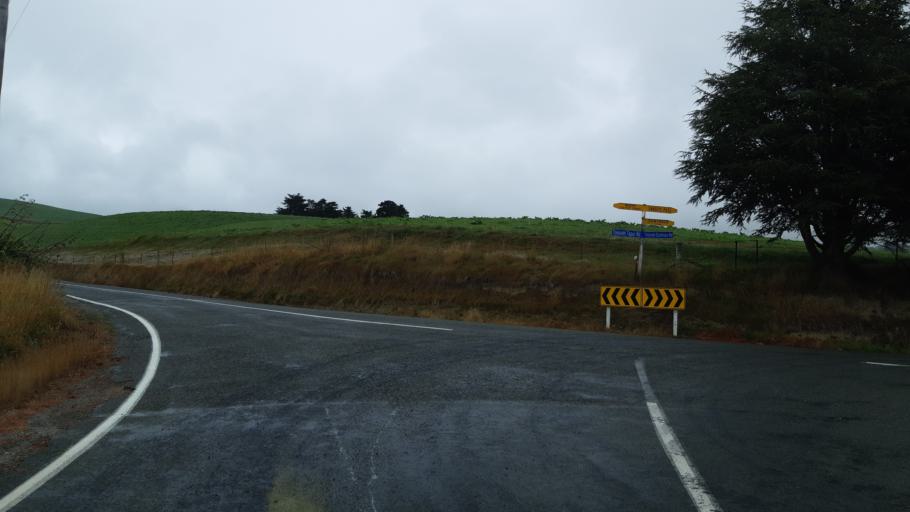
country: NZ
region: Otago
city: Oamaru
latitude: -44.9618
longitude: 170.6452
